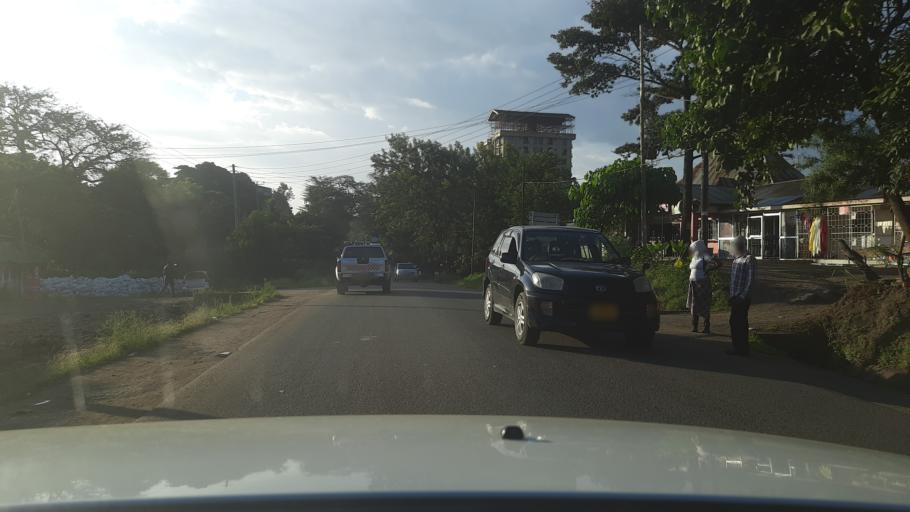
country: TZ
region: Arusha
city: Arusha
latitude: -3.3797
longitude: 36.7065
